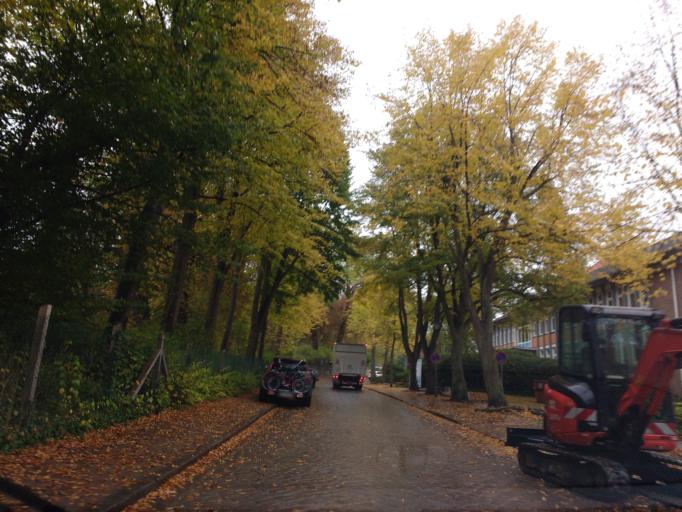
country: DE
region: Schleswig-Holstein
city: Eutin
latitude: 54.1344
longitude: 10.6196
